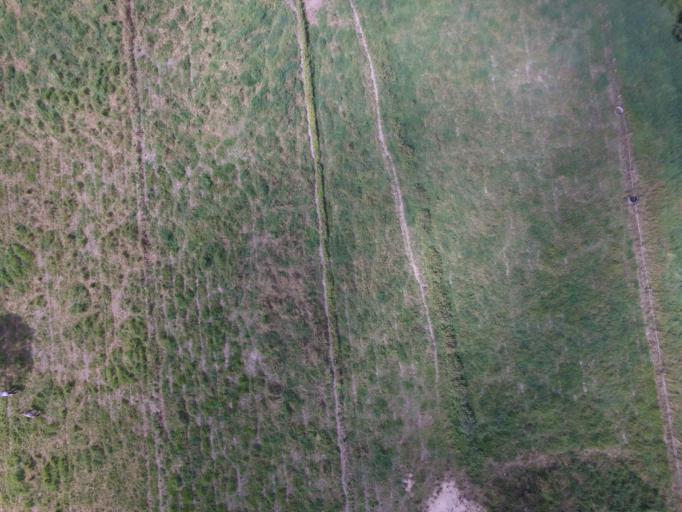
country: AU
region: Queensland
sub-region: Tablelands
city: Atherton
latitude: -17.3021
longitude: 145.4566
